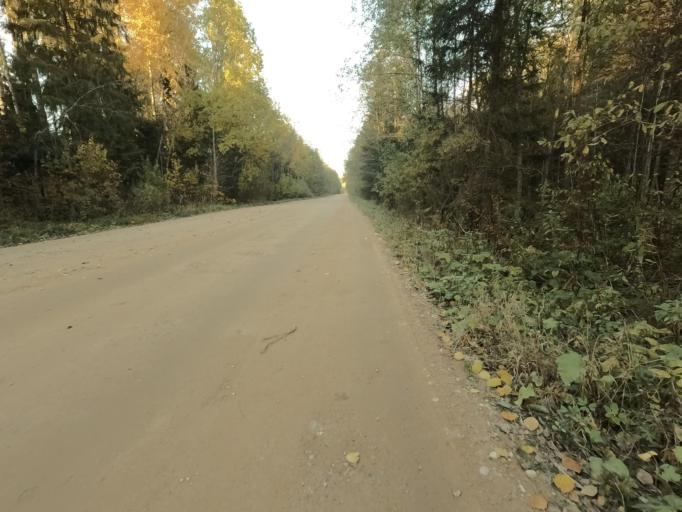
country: RU
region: Leningrad
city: Lyuban'
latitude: 58.9879
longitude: 31.1010
